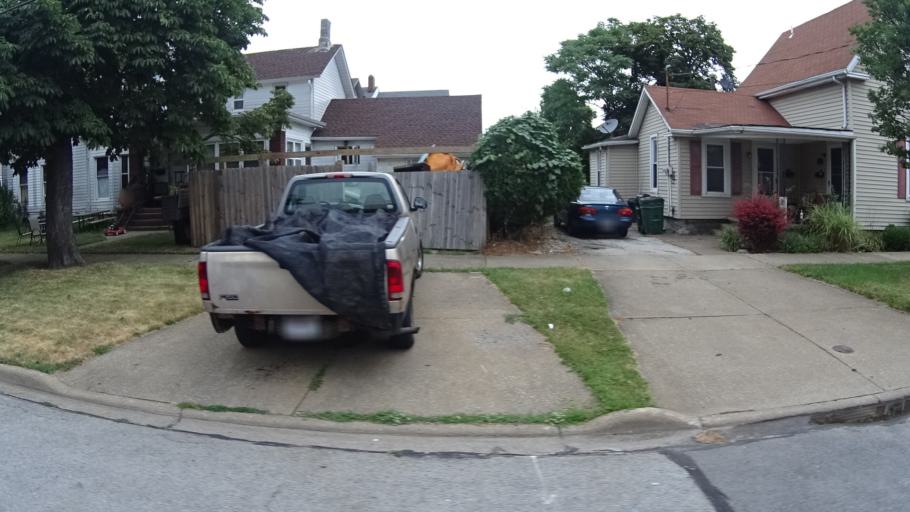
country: US
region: Ohio
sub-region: Erie County
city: Sandusky
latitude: 41.4523
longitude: -82.7146
